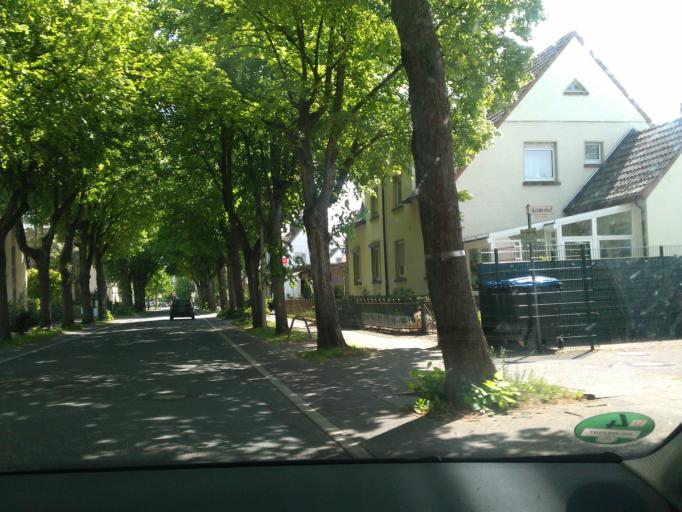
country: DE
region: North Rhine-Westphalia
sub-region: Regierungsbezirk Dusseldorf
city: Hilden
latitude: 51.1577
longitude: 6.9458
